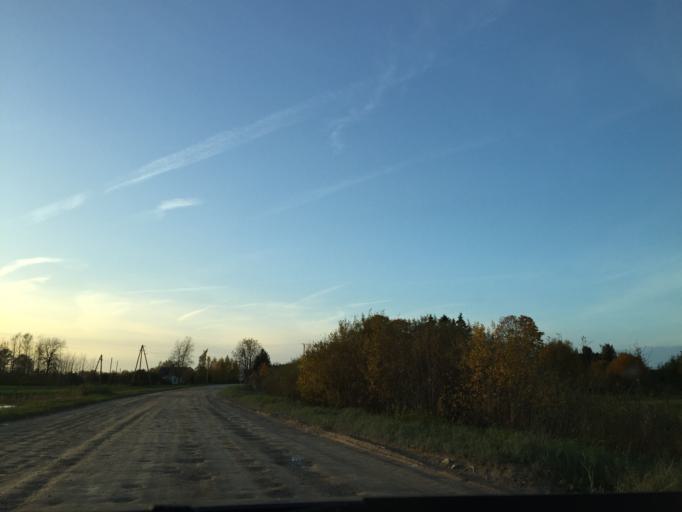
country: LV
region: Malpils
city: Malpils
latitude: 56.8925
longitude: 24.9366
